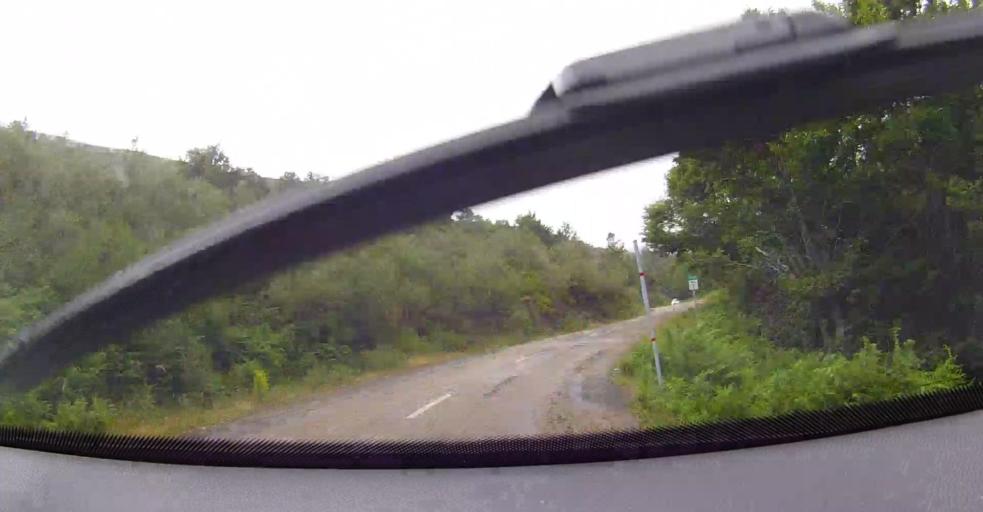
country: ES
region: Castille and Leon
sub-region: Provincia de Leon
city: Puebla de Lillo
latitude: 43.0612
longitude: -5.2746
